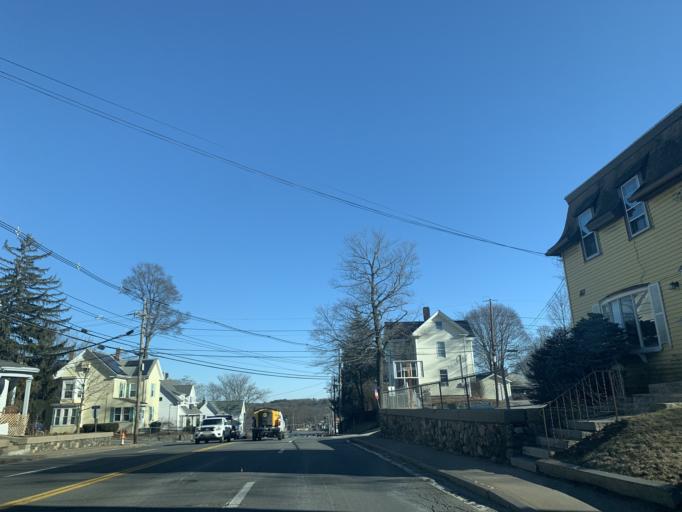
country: US
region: Massachusetts
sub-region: Middlesex County
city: Marlborough
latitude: 42.3511
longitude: -71.5388
